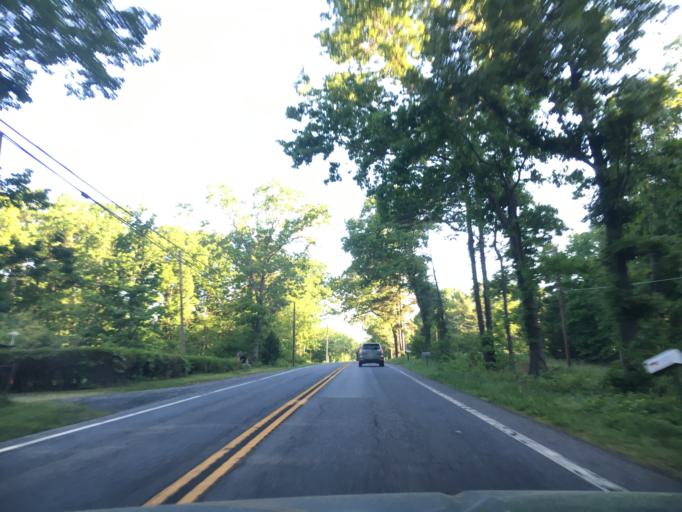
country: US
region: Virginia
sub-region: Campbell County
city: Rustburg
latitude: 37.2537
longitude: -79.1200
